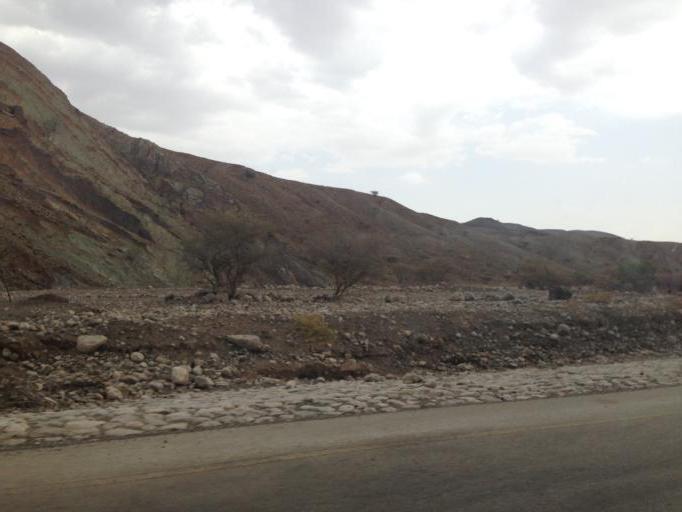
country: OM
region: Ash Sharqiyah
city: Badiyah
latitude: 22.5616
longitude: 59.0288
